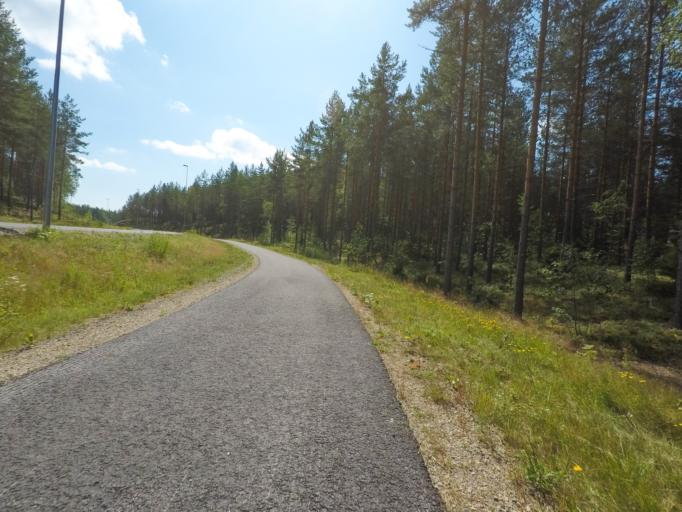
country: FI
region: Southern Savonia
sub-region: Mikkeli
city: Puumala
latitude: 61.5106
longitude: 28.1653
